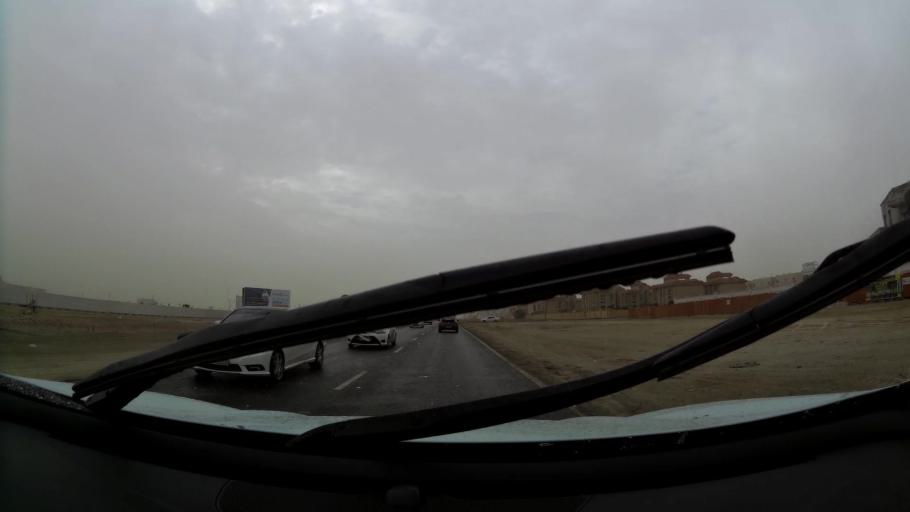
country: AE
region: Abu Dhabi
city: Abu Dhabi
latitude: 24.4366
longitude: 54.6028
